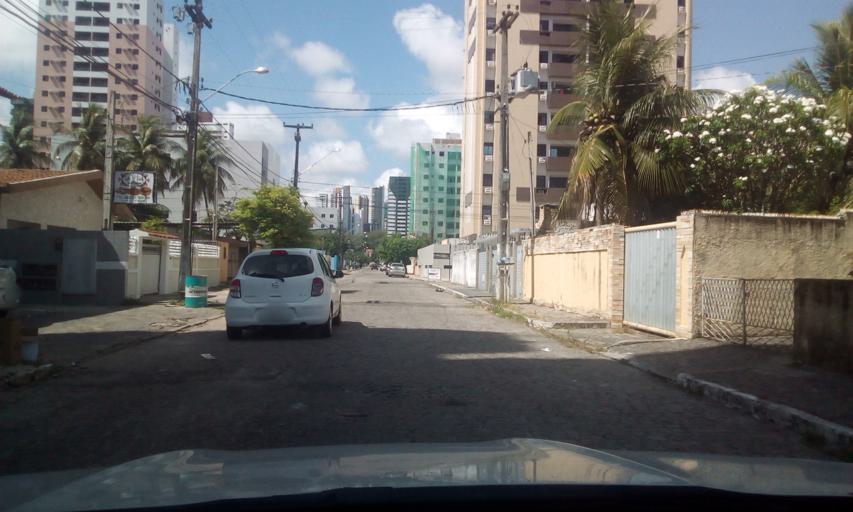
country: BR
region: Paraiba
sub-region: Joao Pessoa
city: Joao Pessoa
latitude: -7.1087
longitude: -34.8286
